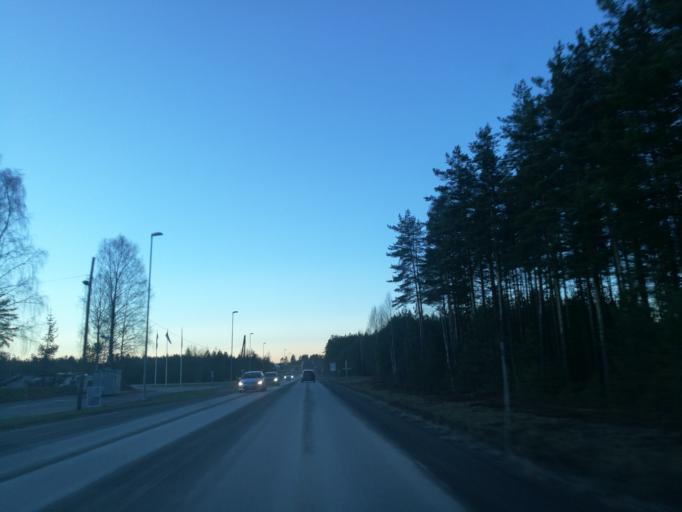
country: SE
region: Vaermland
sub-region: Eda Kommun
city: Charlottenberg
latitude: 59.9336
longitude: 12.2308
